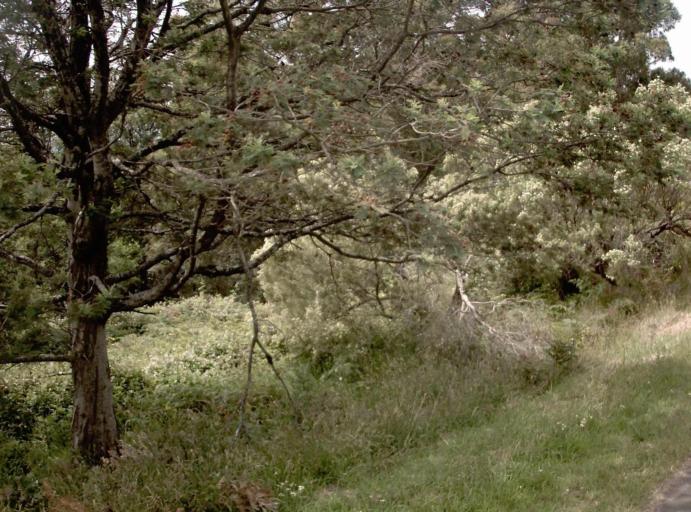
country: AU
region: Victoria
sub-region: Latrobe
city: Traralgon
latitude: -38.3707
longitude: 146.6909
